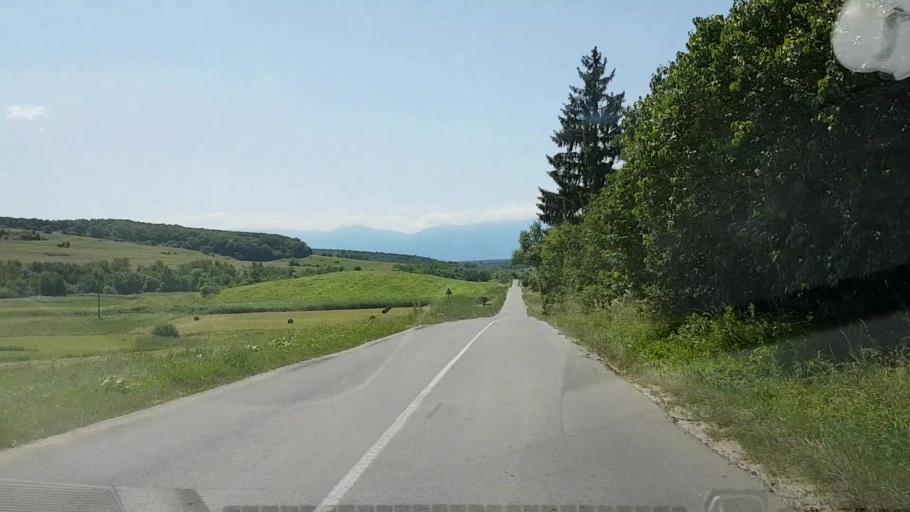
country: RO
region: Brasov
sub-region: Comuna Cincu
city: Cincu
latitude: 45.9070
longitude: 24.8116
